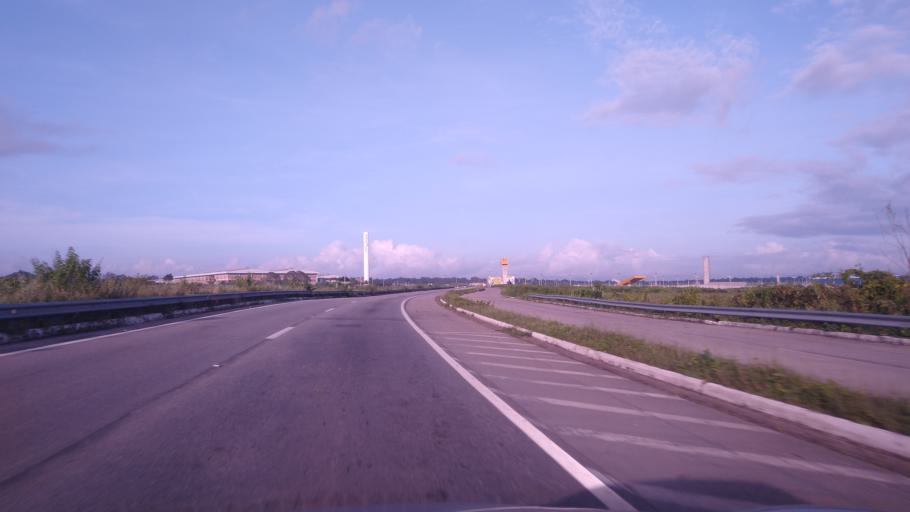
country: BR
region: Ceara
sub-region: Pacajus
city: Pacajus
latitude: -4.1615
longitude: -38.4848
